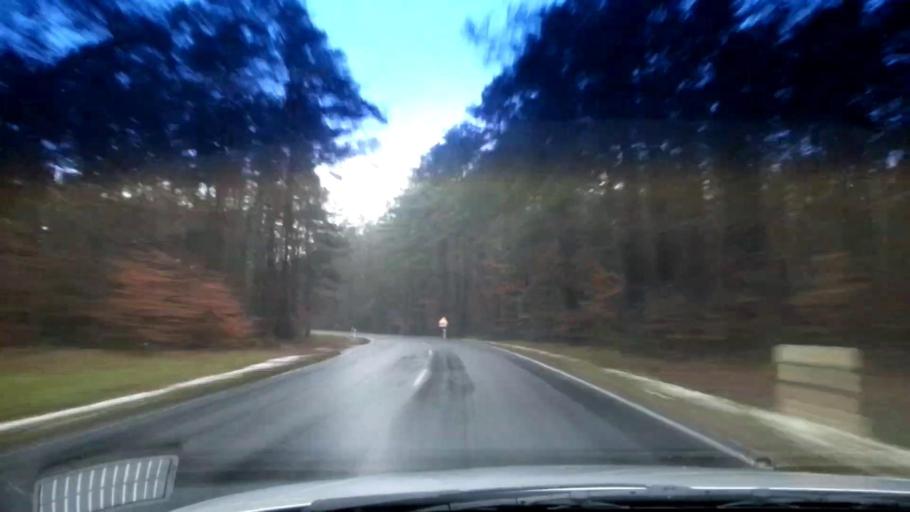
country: DE
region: Bavaria
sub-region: Upper Franconia
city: Oberhaid
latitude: 49.9537
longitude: 10.8134
